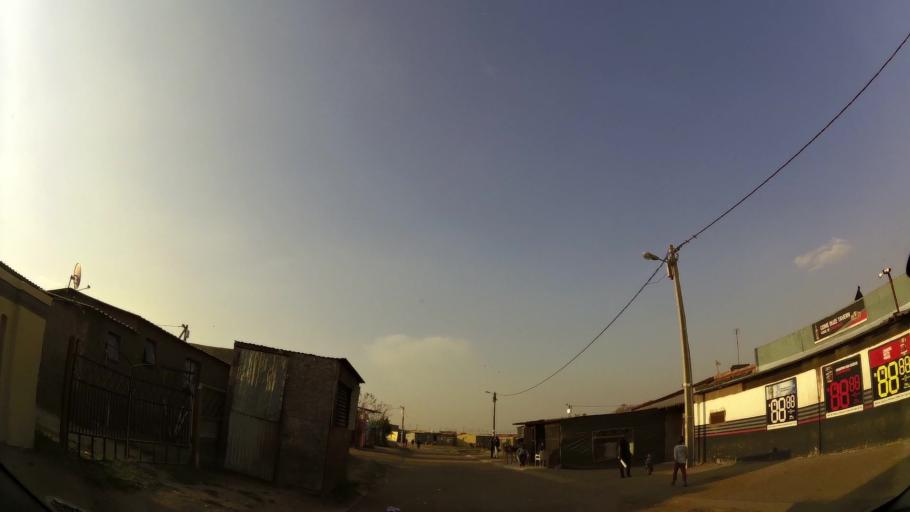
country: ZA
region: Gauteng
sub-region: Ekurhuleni Metropolitan Municipality
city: Benoni
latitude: -26.1534
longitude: 28.3834
